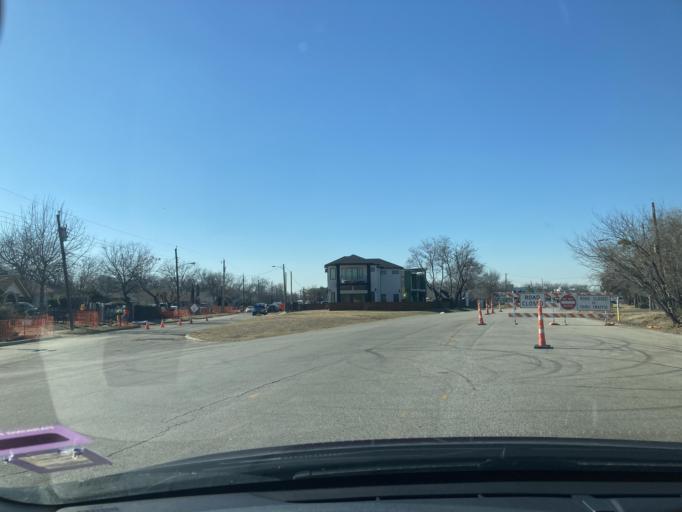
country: US
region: Texas
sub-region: Dallas County
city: Dallas
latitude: 32.7888
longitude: -96.8438
